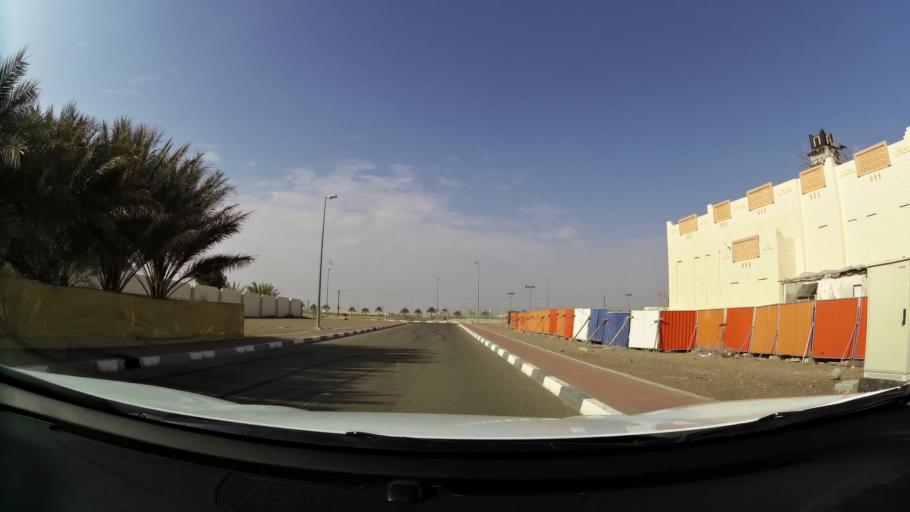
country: AE
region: Abu Dhabi
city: Al Ain
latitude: 24.0898
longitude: 55.8649
